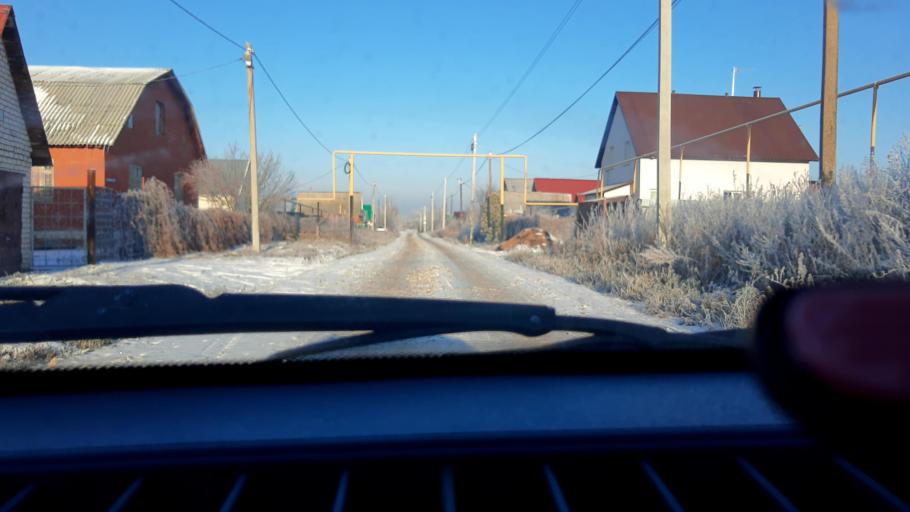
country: RU
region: Bashkortostan
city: Mikhaylovka
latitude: 54.8694
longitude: 55.7603
